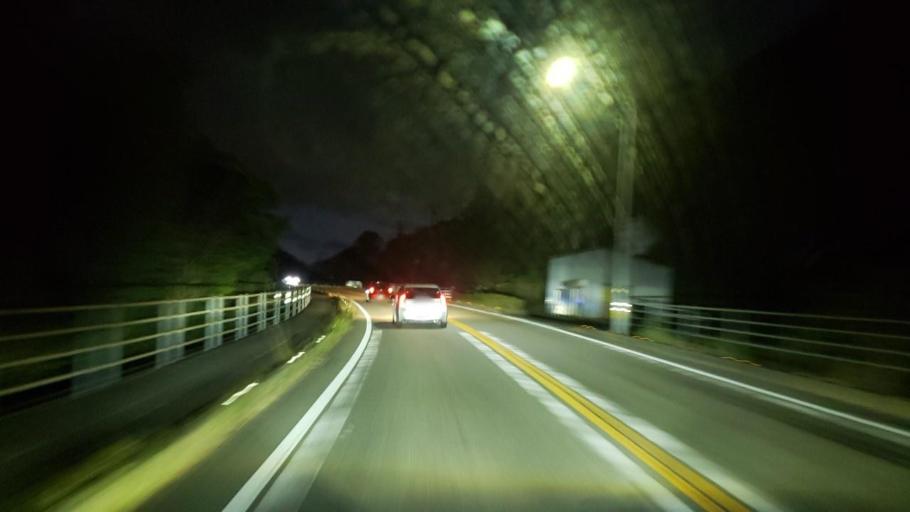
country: JP
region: Tokushima
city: Narutocho-mitsuishi
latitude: 34.2112
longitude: 134.5609
